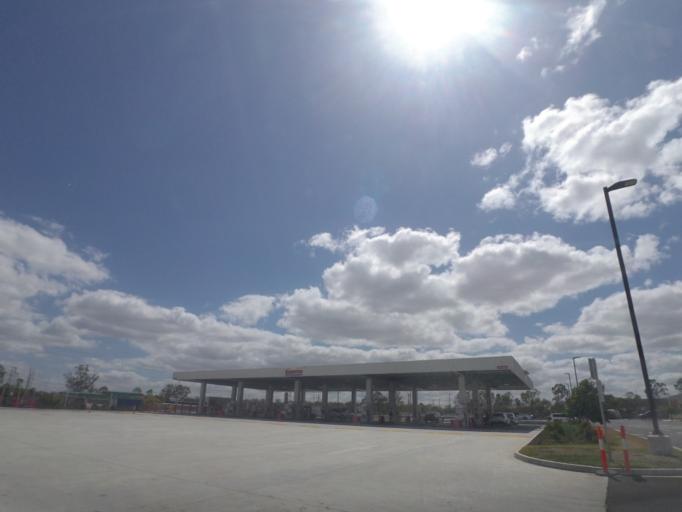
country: AU
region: Queensland
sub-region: Ipswich
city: Bundamba
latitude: -27.5896
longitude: 152.8205
